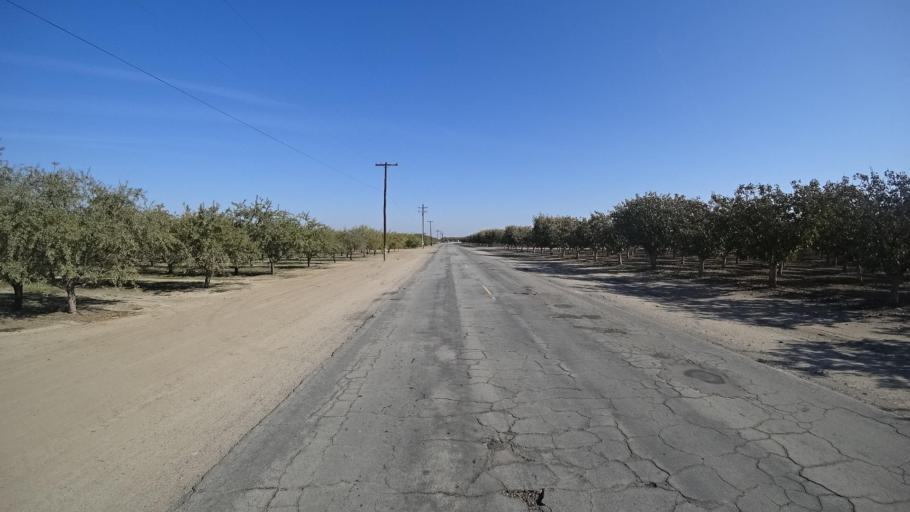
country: US
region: California
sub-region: Kern County
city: Wasco
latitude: 35.6524
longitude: -119.3365
